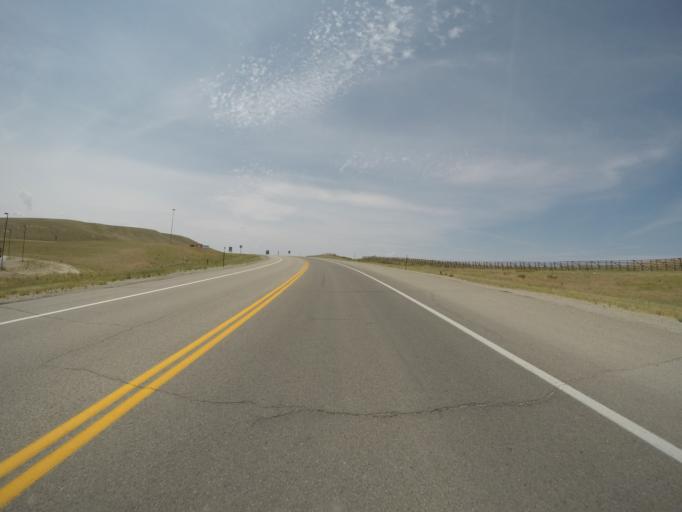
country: US
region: Wyoming
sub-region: Lincoln County
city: Kemmerer
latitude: 41.7735
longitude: -110.5508
